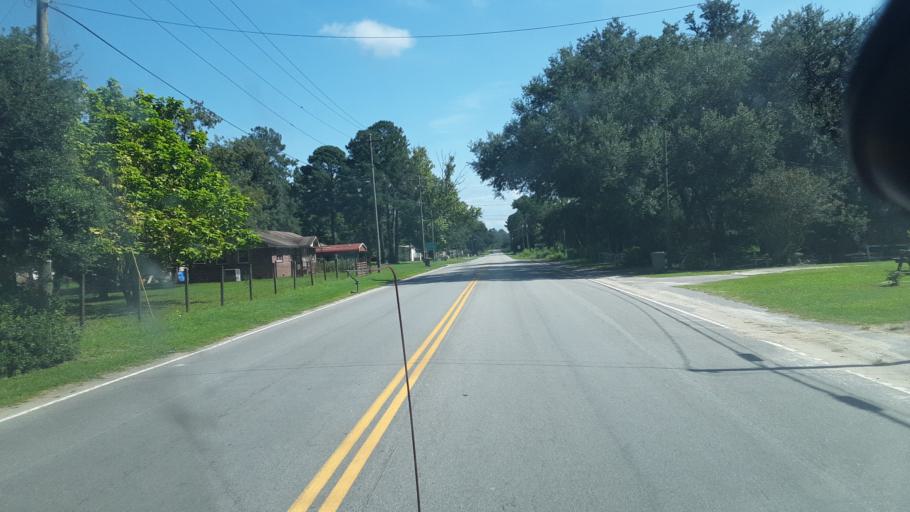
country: US
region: South Carolina
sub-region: Hampton County
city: Varnville
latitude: 32.8574
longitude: -81.0734
